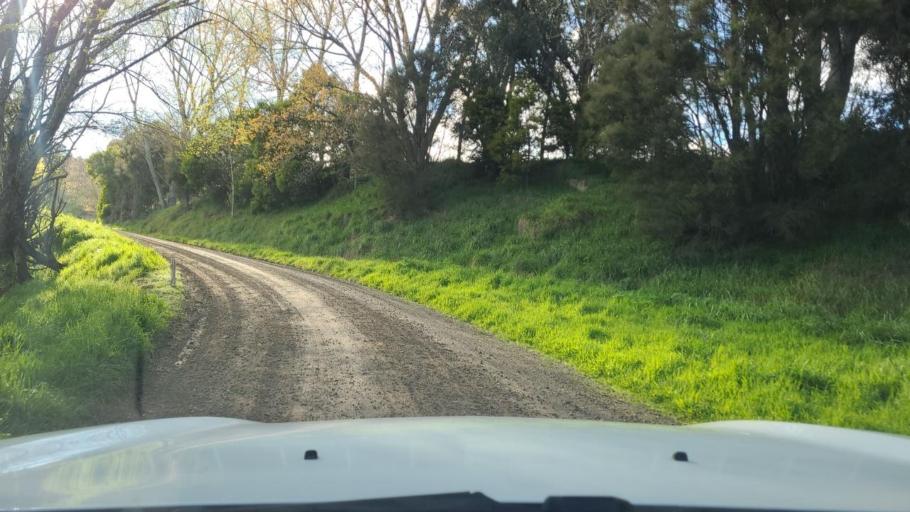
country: NZ
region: Wellington
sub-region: Masterton District
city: Masterton
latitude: -41.2130
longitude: 175.6781
